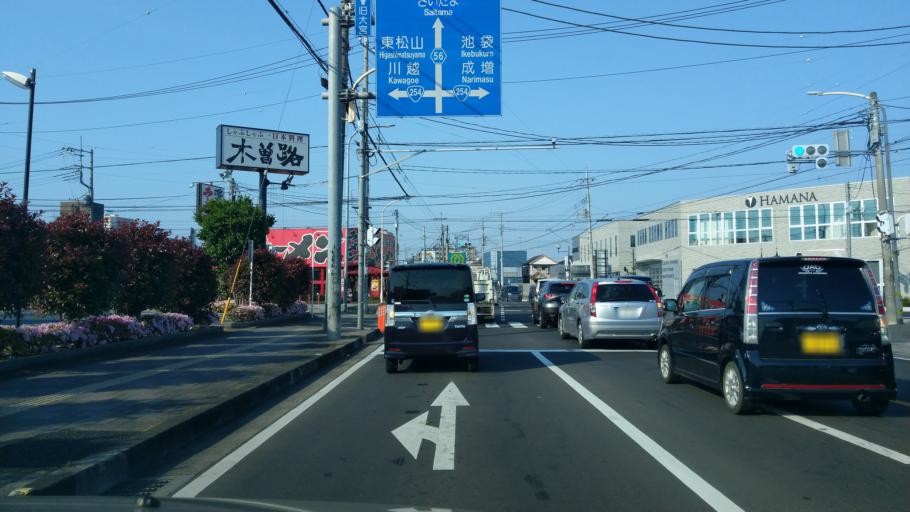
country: JP
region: Saitama
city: Kamifukuoka
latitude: 35.8651
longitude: 139.5082
